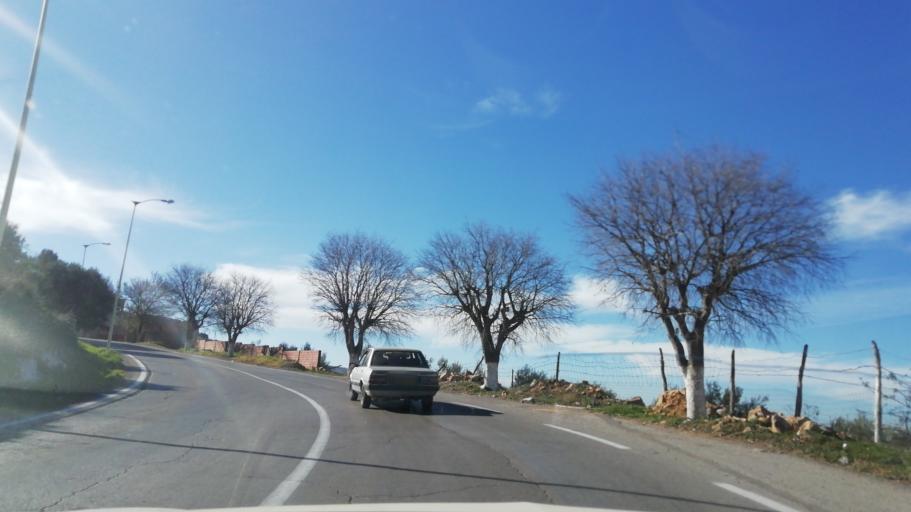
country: DZ
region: Tlemcen
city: Mansoura
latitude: 34.8593
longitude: -1.3398
